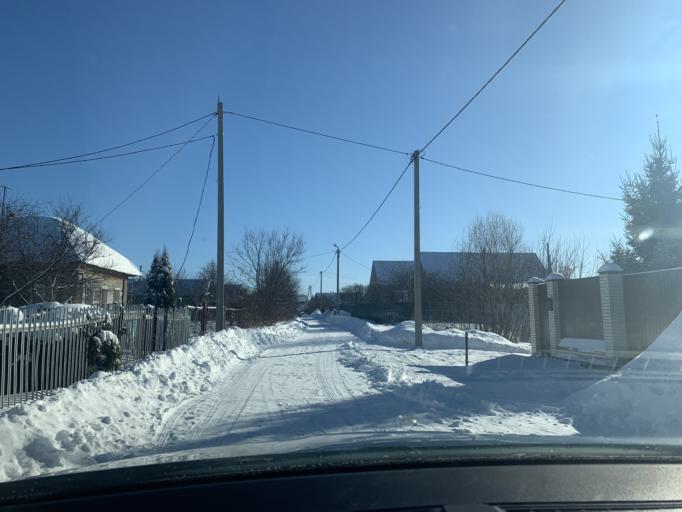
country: RU
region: Jaroslavl
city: Tunoshna
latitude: 57.6523
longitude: 40.0618
